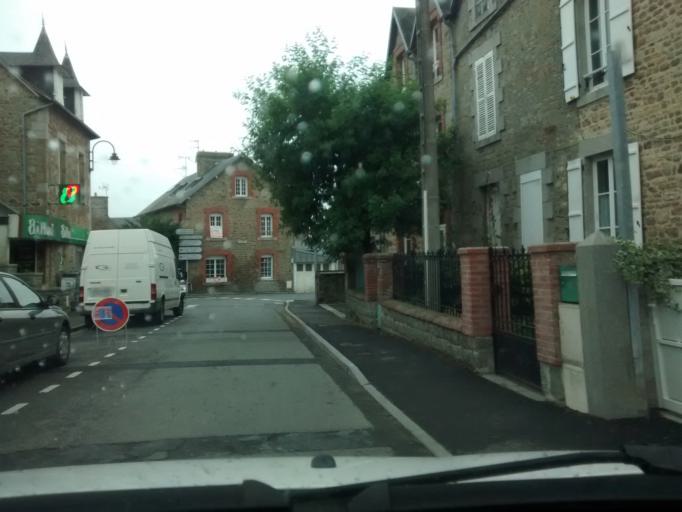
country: FR
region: Lower Normandy
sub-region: Departement de la Manche
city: Jullouville
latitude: 48.7502
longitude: -1.5601
